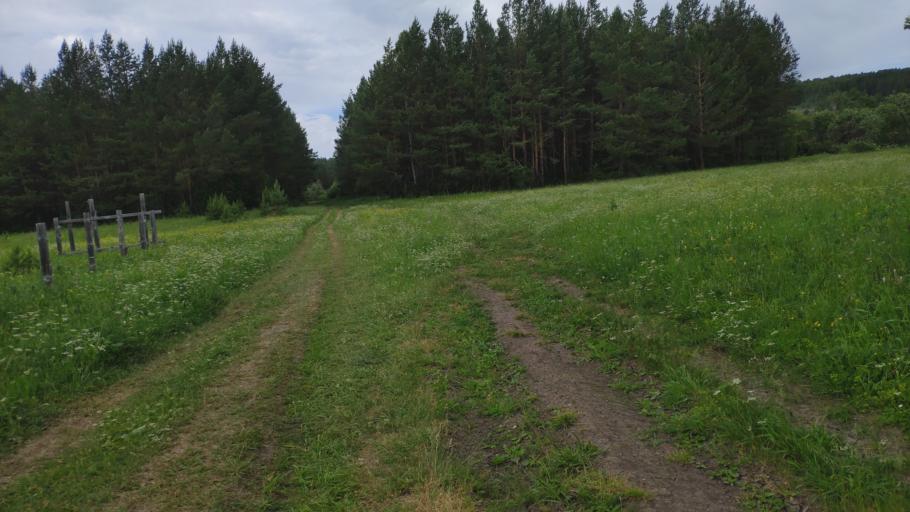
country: RU
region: Bashkortostan
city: Abzakovo
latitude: 53.8172
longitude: 58.6347
